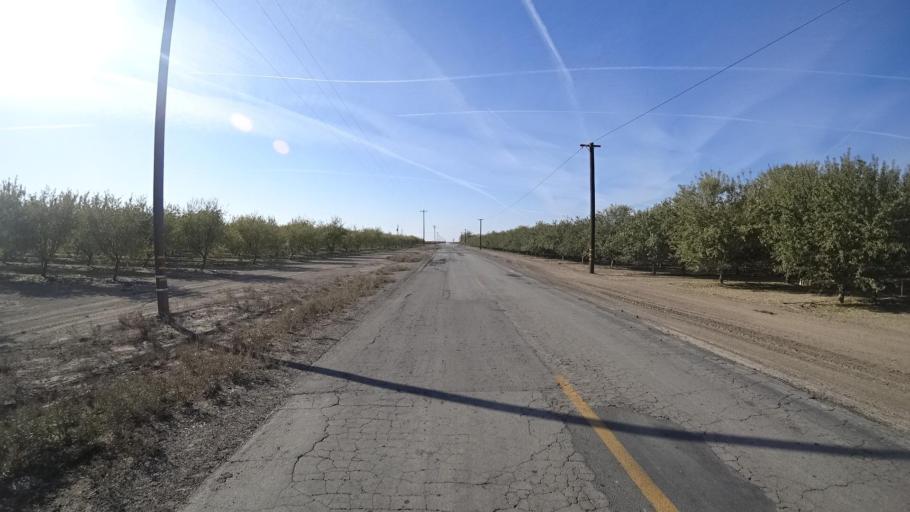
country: US
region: California
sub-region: Kern County
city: Wasco
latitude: 35.7032
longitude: -119.3814
